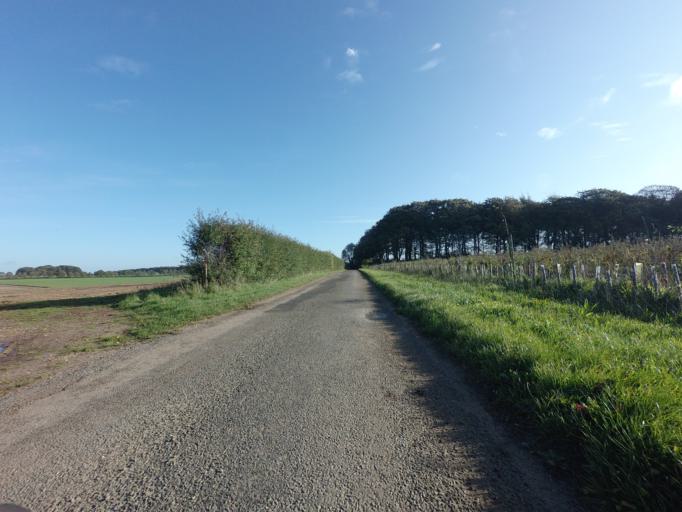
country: GB
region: England
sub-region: Norfolk
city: Dersingham
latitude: 52.8261
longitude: 0.5555
